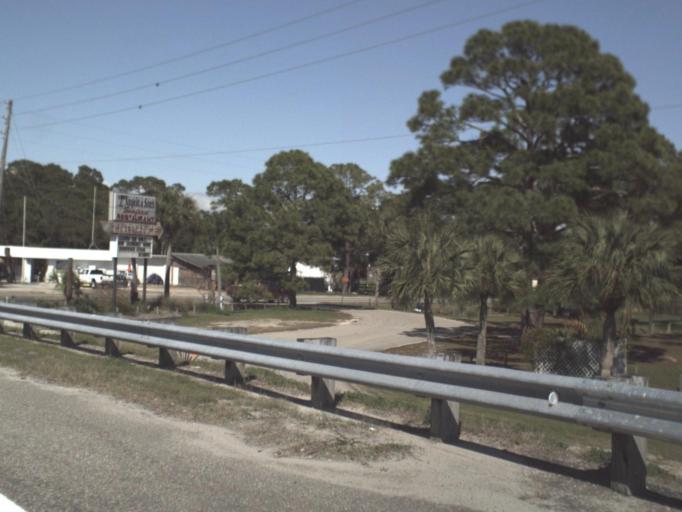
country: US
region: Florida
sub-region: Wakulla County
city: Crawfordville
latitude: 29.9780
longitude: -84.3832
